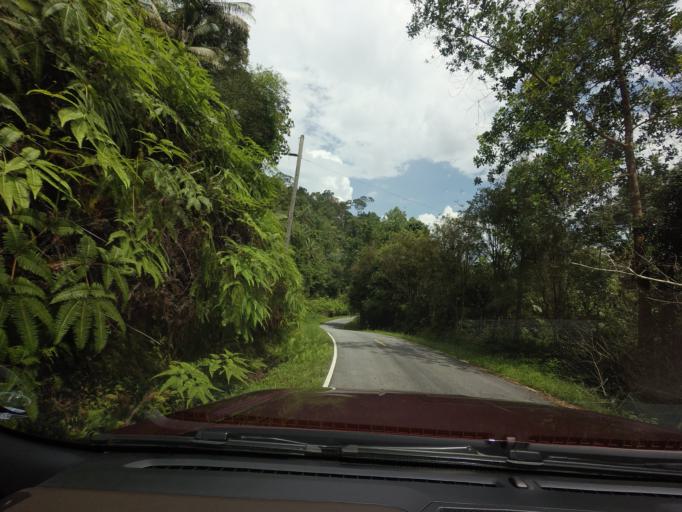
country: TH
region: Narathiwat
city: Sukhirin
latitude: 5.9331
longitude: 101.6503
